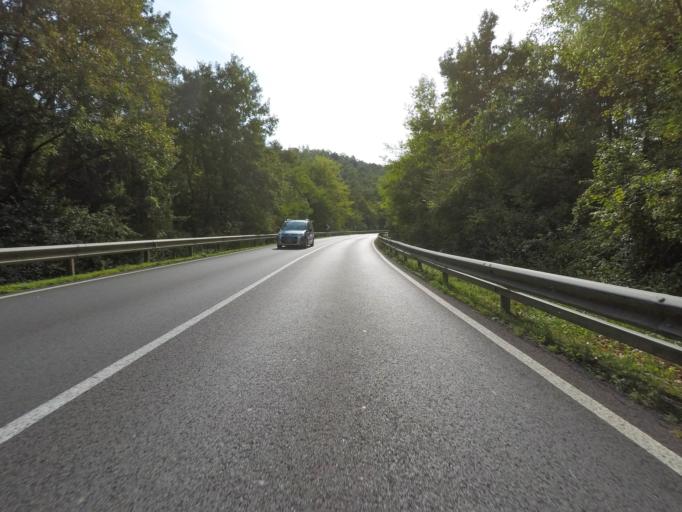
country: IT
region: Tuscany
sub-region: Provincia di Siena
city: Rosia
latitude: 43.1922
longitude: 11.2779
